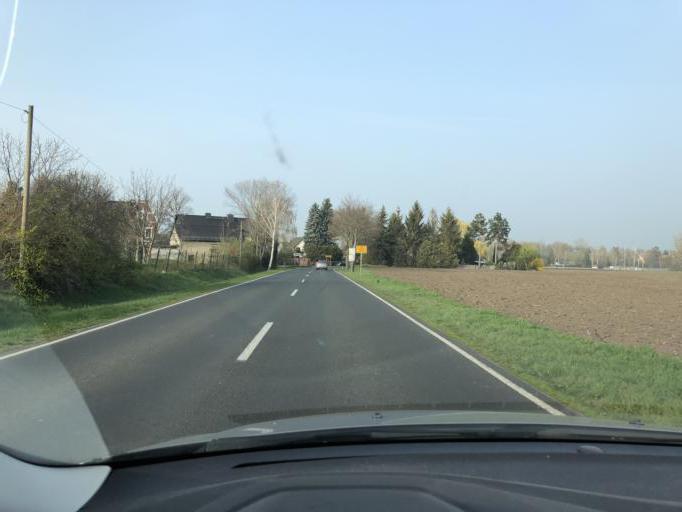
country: DE
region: Saxony-Anhalt
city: Zorbig
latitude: 51.6224
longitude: 12.1071
